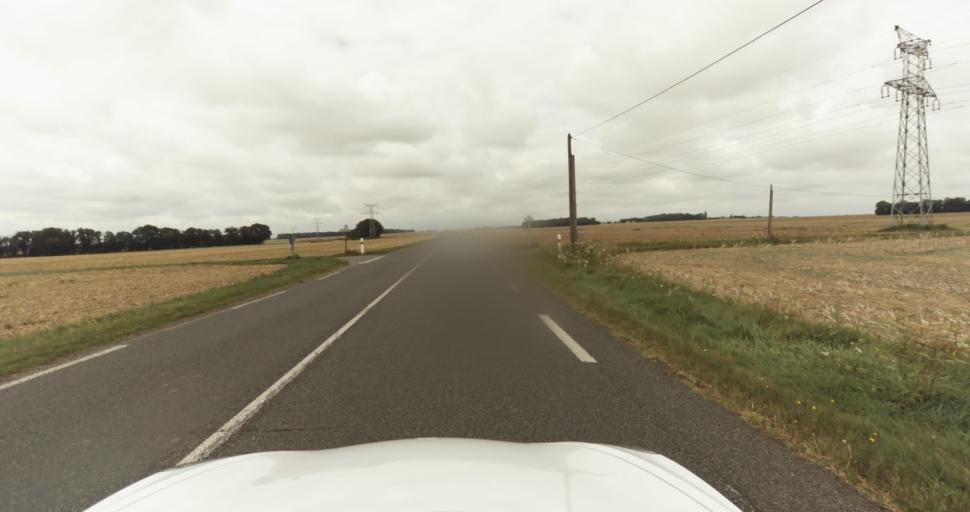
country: FR
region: Haute-Normandie
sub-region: Departement de l'Eure
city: Claville
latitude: 49.0369
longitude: 1.0415
